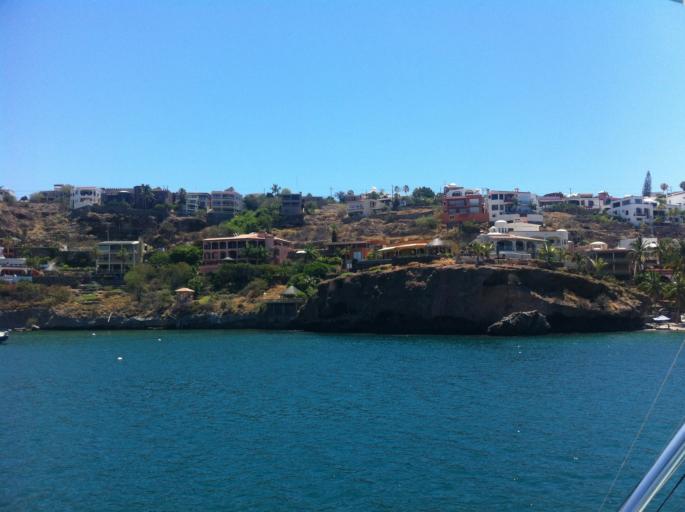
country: MX
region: Sonora
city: Heroica Guaymas
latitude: 27.9422
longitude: -111.0596
